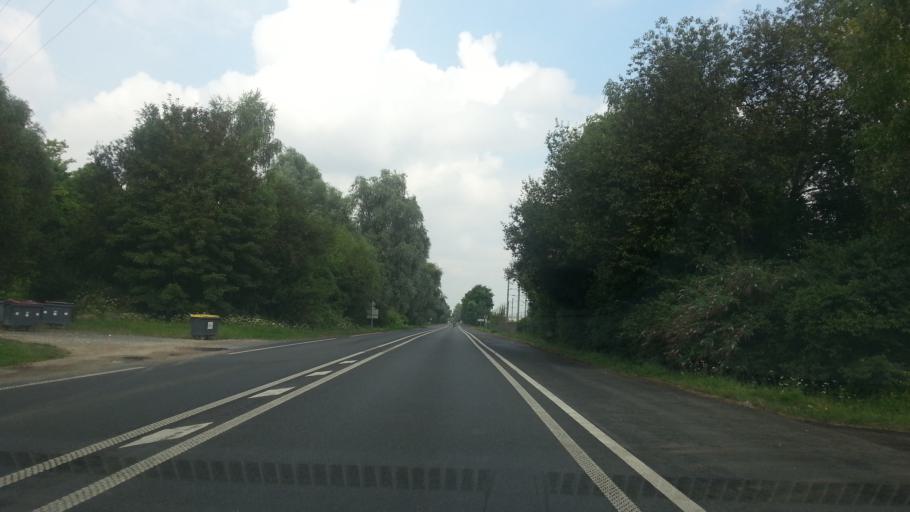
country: FR
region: Picardie
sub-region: Departement de l'Oise
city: Saint-Maximin
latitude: 49.2256
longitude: 2.4303
